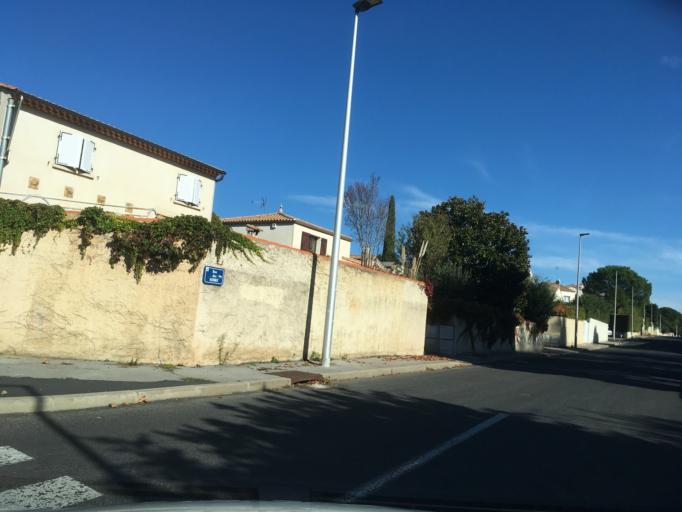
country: FR
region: Languedoc-Roussillon
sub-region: Departement de l'Herault
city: Saint-Jean-de-Vedas
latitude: 43.5995
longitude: 3.8351
